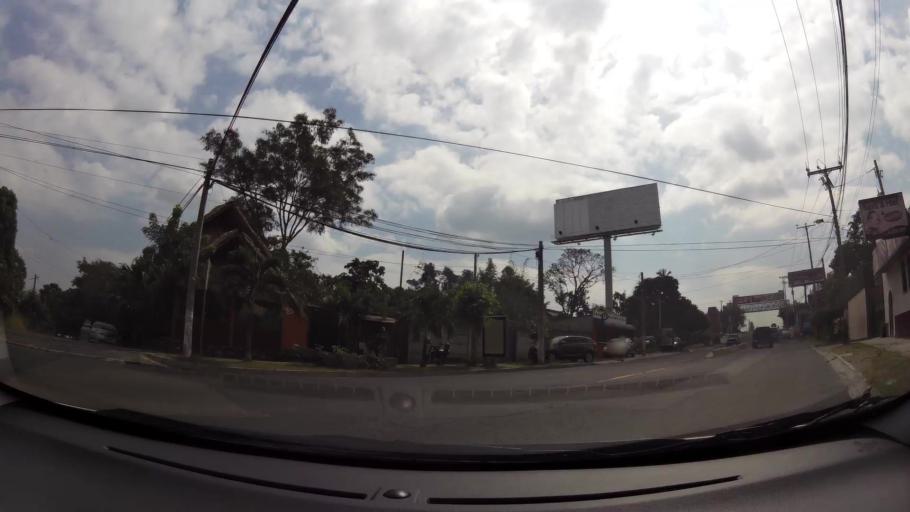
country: SV
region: San Salvador
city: Mejicanos
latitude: 13.7150
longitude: -89.2471
